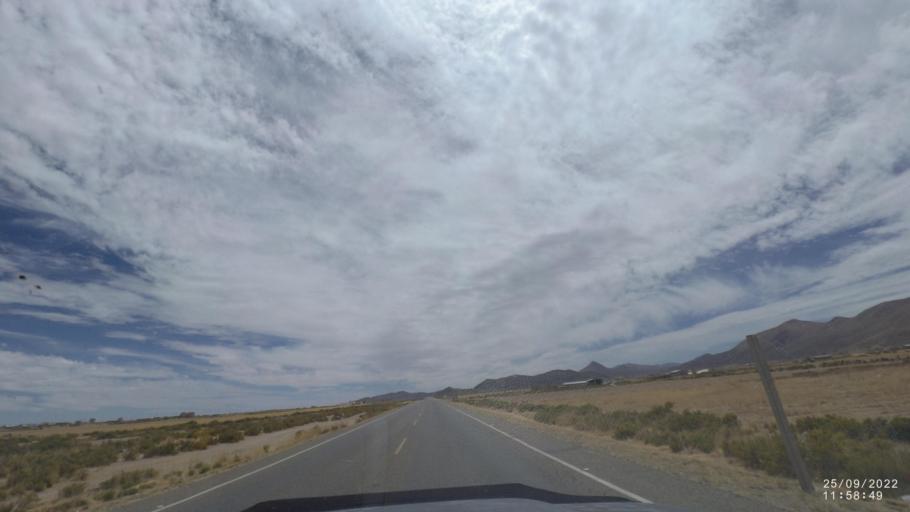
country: BO
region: Oruro
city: Challapata
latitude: -18.7980
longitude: -66.8412
